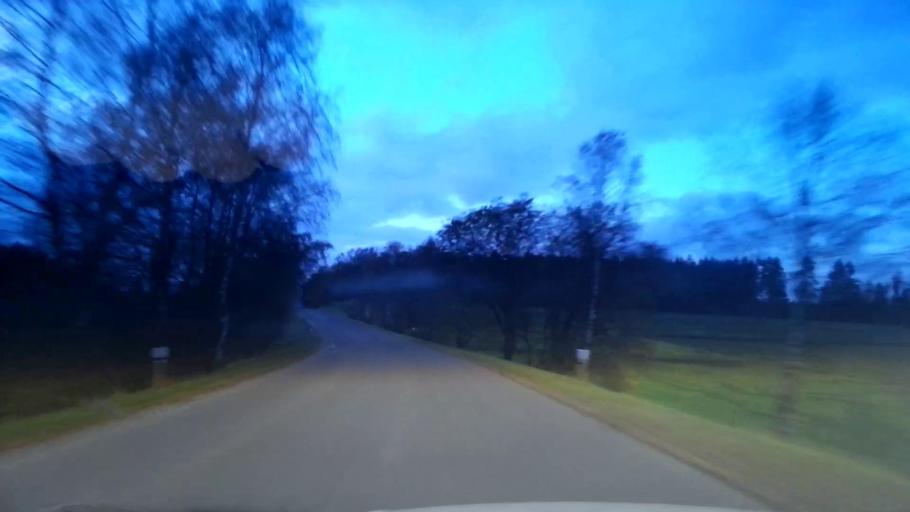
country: DE
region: Bavaria
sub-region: Upper Palatinate
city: Waldershof
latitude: 49.9688
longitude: 12.0828
